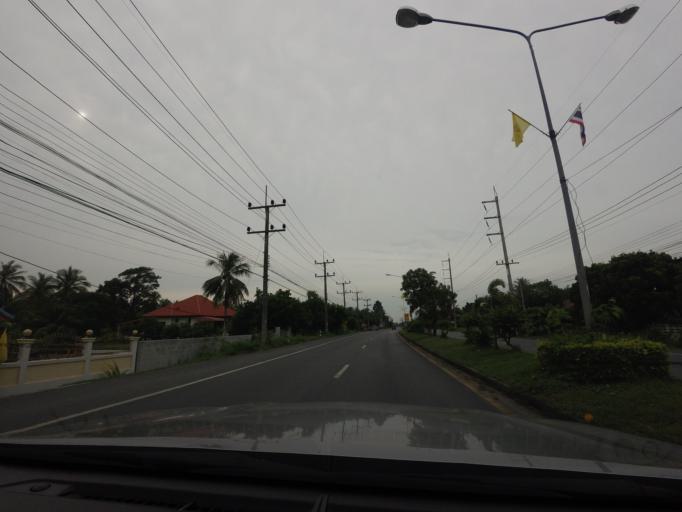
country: TH
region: Songkhla
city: Sathing Phra
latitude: 7.4878
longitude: 100.4345
